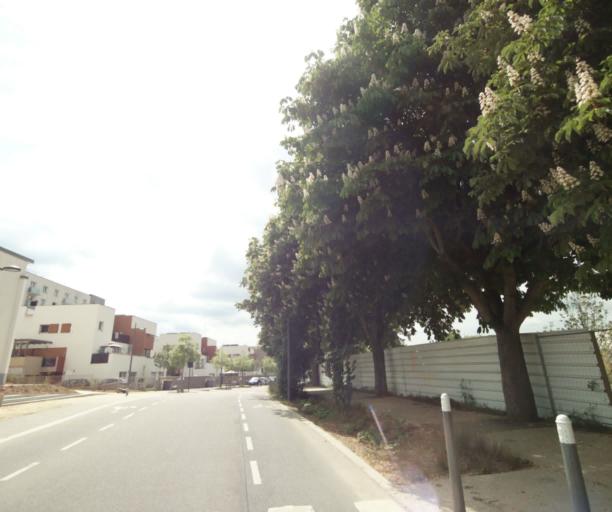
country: FR
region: Ile-de-France
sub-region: Departement des Yvelines
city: Les Mureaux
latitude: 48.9831
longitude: 1.9157
